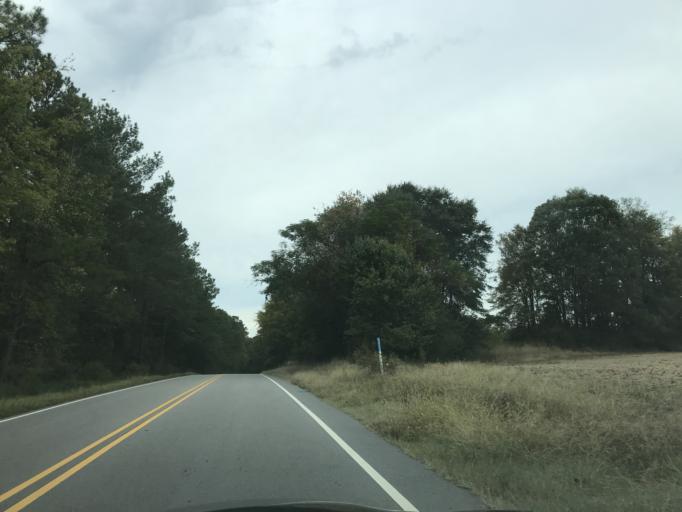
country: US
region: North Carolina
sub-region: Wake County
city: Knightdale
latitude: 35.8145
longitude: -78.4984
